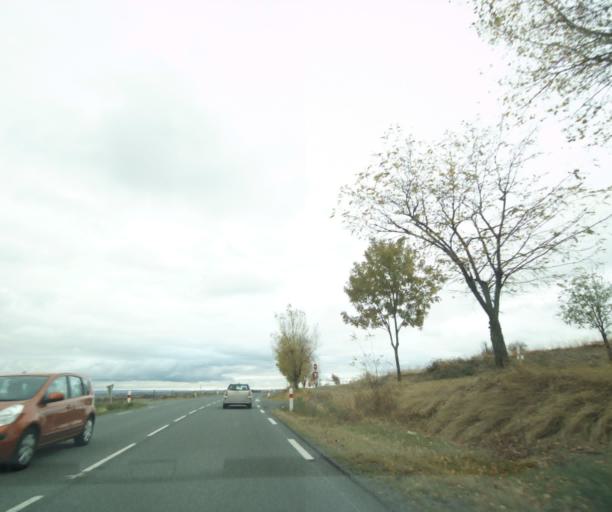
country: FR
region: Auvergne
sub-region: Departement du Puy-de-Dome
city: Pont-du-Chateau
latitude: 45.8024
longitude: 3.2266
